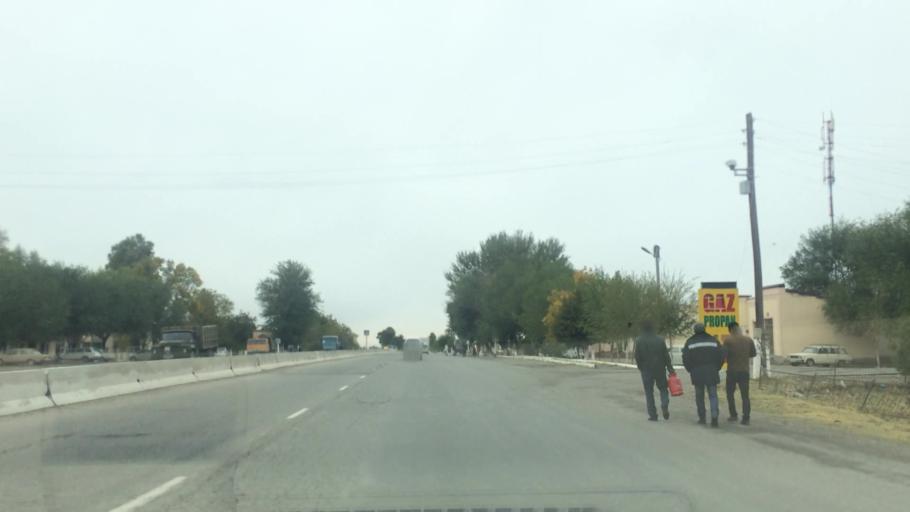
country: UZ
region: Samarqand
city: Bulung'ur
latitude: 39.7396
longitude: 67.1846
